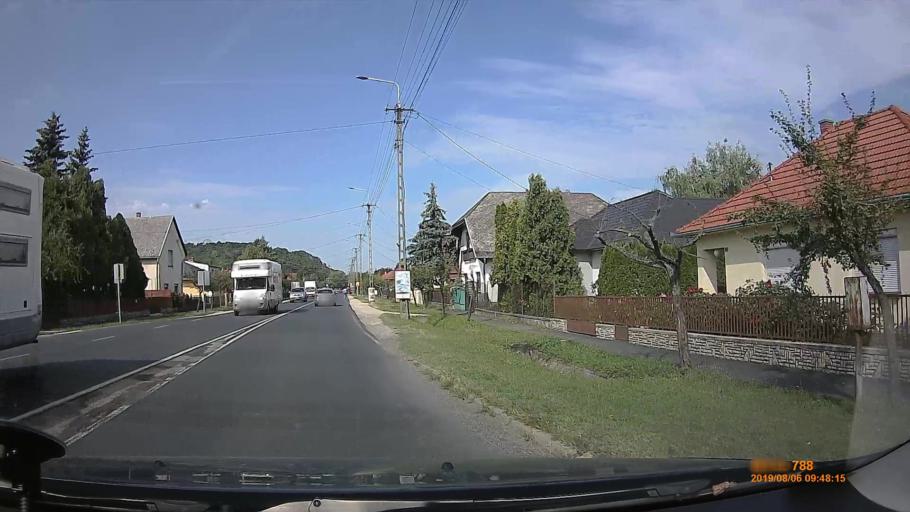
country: HU
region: Somogy
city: Balatonlelle
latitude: 46.7830
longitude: 17.6700
